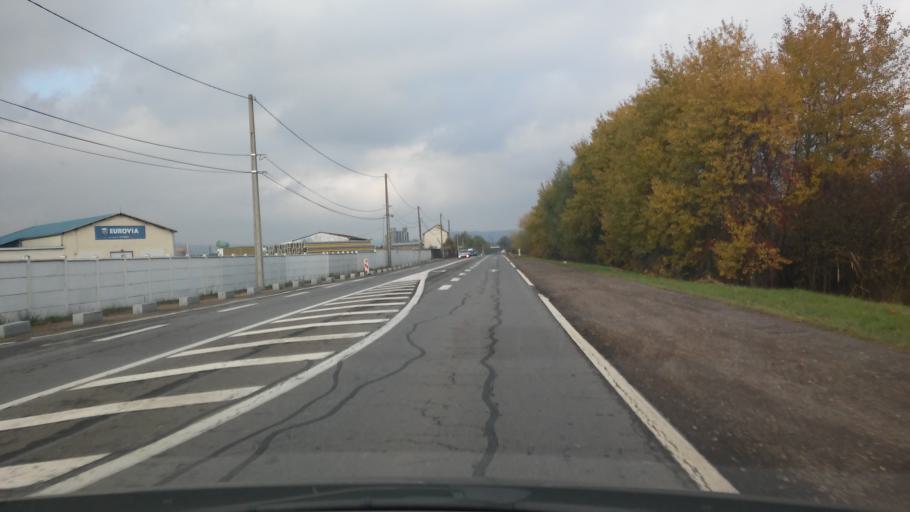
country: FR
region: Lorraine
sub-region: Departement de la Moselle
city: Uckange
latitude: 49.3188
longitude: 6.1559
